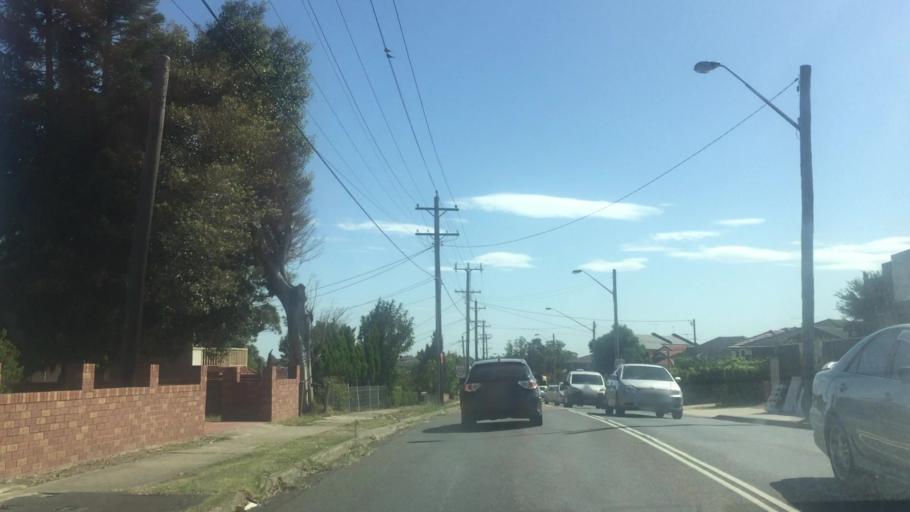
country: AU
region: New South Wales
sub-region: Holroyd
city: Merrylands
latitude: -33.8267
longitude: 150.9828
